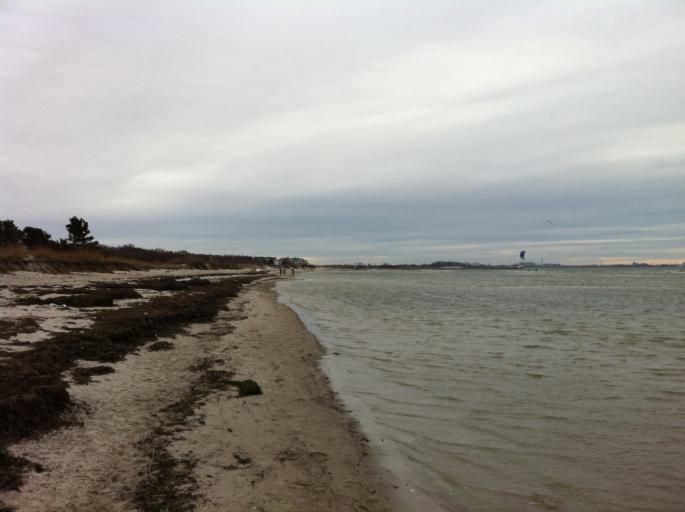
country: SE
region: Skane
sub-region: Lomma Kommun
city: Lomma
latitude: 55.6844
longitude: 13.0567
